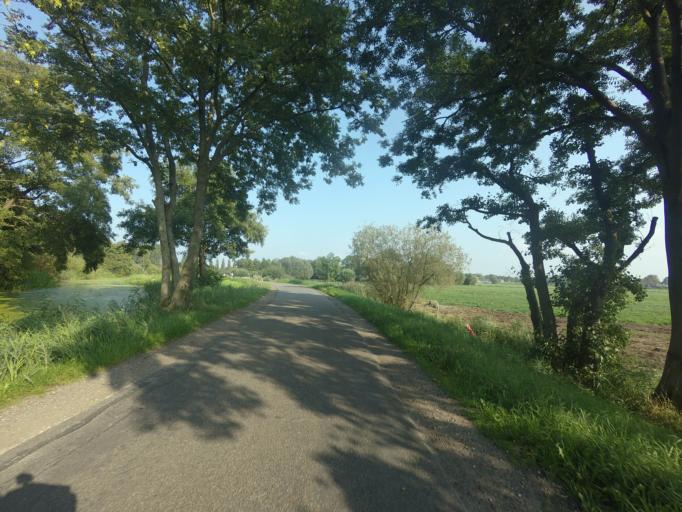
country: NL
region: Groningen
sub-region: Gemeente Haren
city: Haren
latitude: 53.1723
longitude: 6.5842
